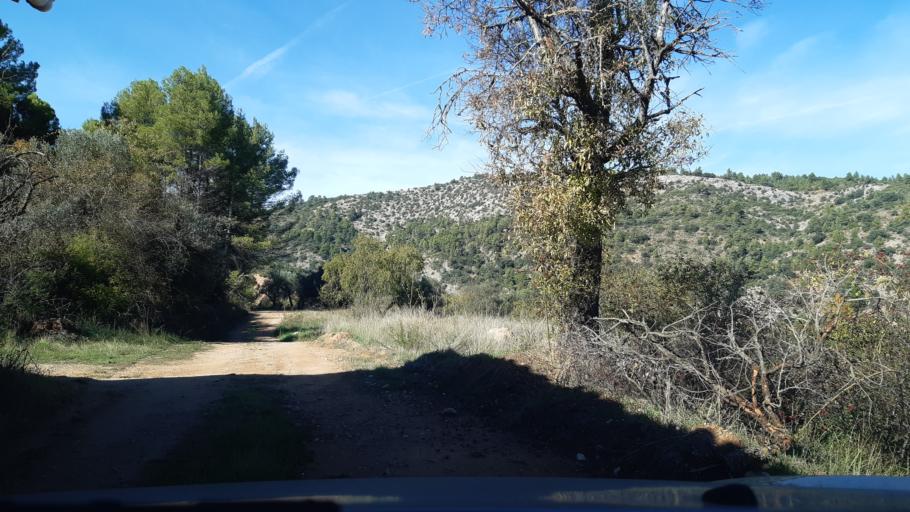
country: ES
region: Aragon
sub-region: Provincia de Teruel
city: Valderrobres
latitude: 40.8405
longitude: 0.2041
